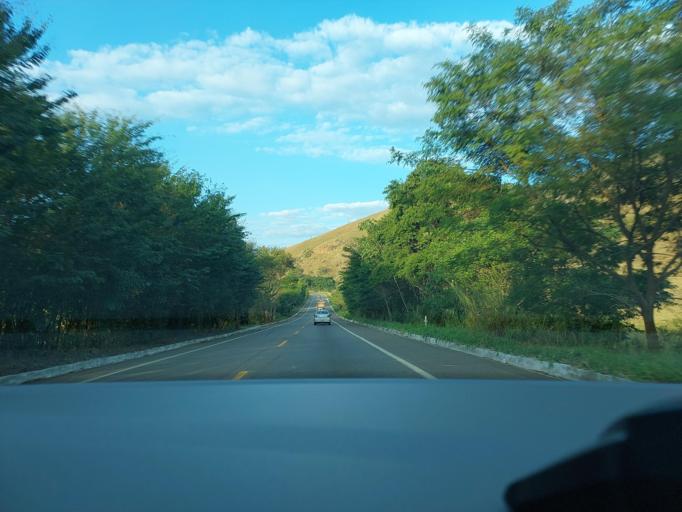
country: BR
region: Minas Gerais
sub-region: Muriae
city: Muriae
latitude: -21.1268
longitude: -42.2389
